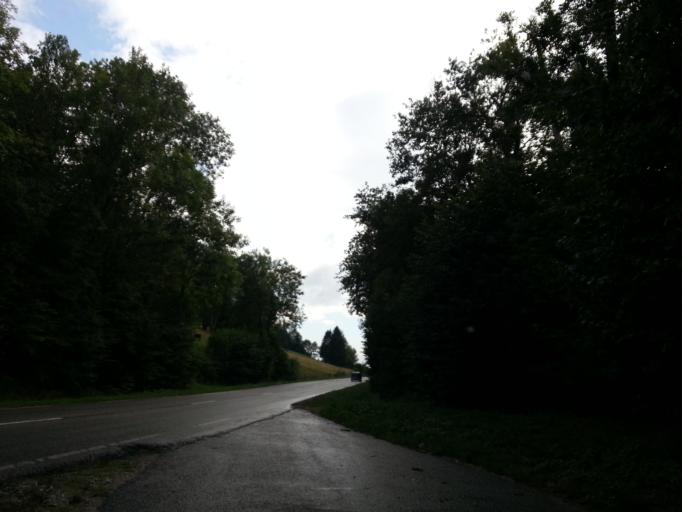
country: FR
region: Rhone-Alpes
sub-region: Departement de la Haute-Savoie
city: Dingy-Saint-Clair
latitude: 45.8843
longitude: 6.2234
